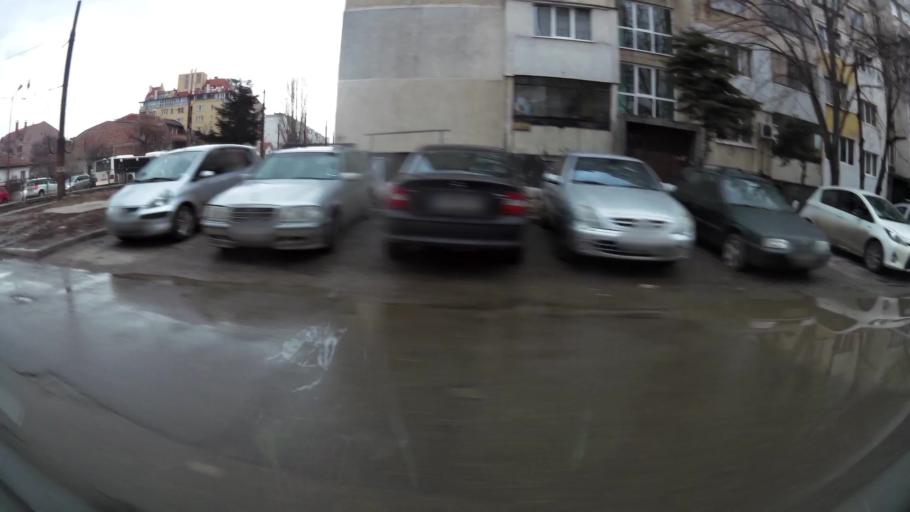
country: BG
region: Sofia-Capital
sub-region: Stolichna Obshtina
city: Sofia
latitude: 42.7303
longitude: 23.2932
